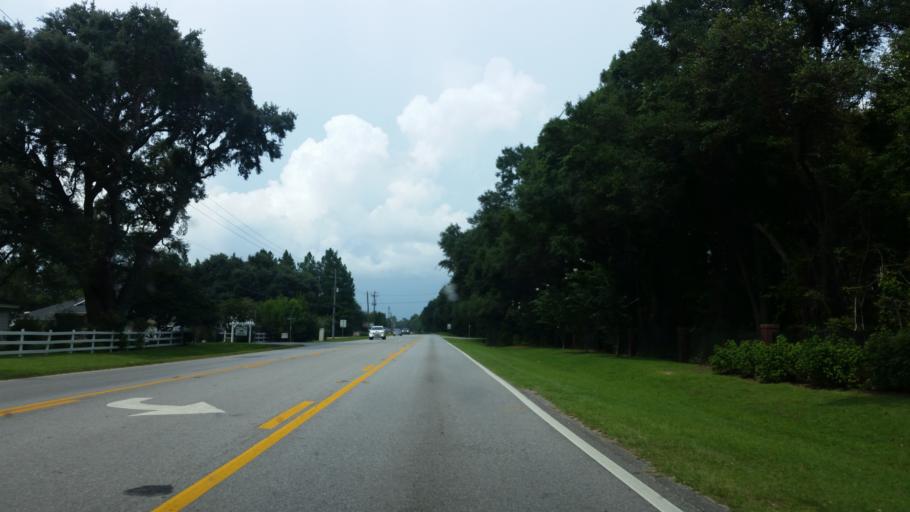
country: US
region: Florida
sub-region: Santa Rosa County
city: Pace
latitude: 30.6286
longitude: -87.1817
